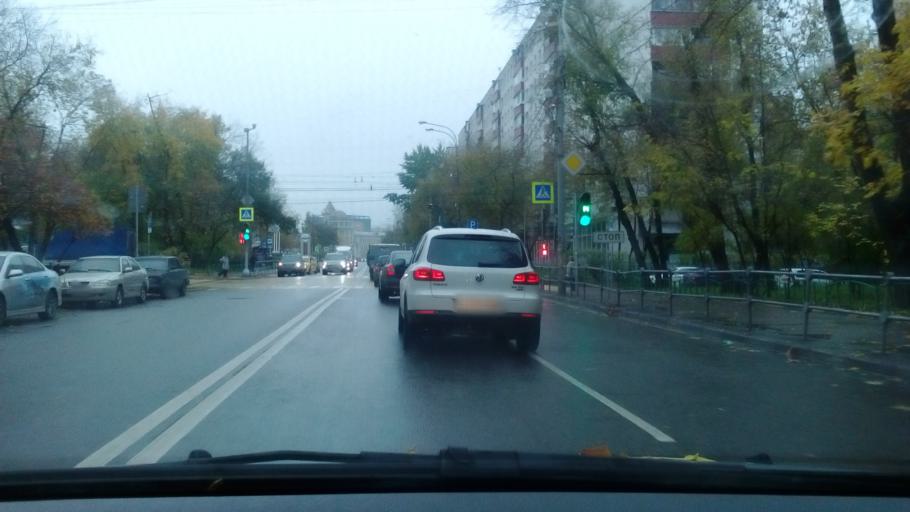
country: RU
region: Moscow
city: Mar'ina Roshcha
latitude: 55.7954
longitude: 37.5765
